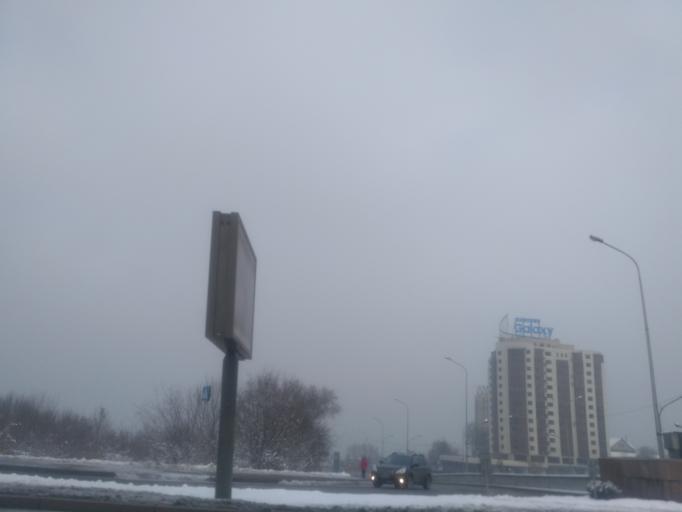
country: KZ
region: Almaty Qalasy
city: Almaty
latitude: 43.2259
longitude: 76.9405
